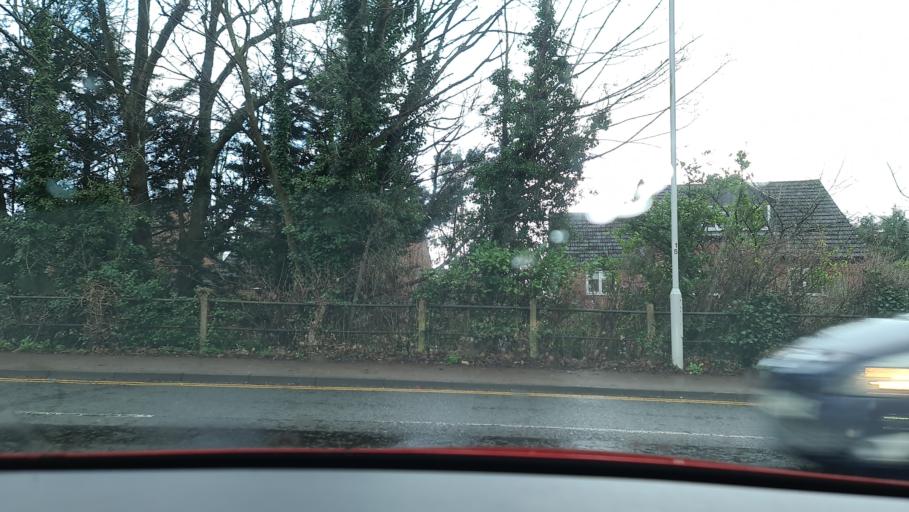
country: GB
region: England
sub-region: Buckinghamshire
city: Buckingham
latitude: 52.0047
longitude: -0.9856
